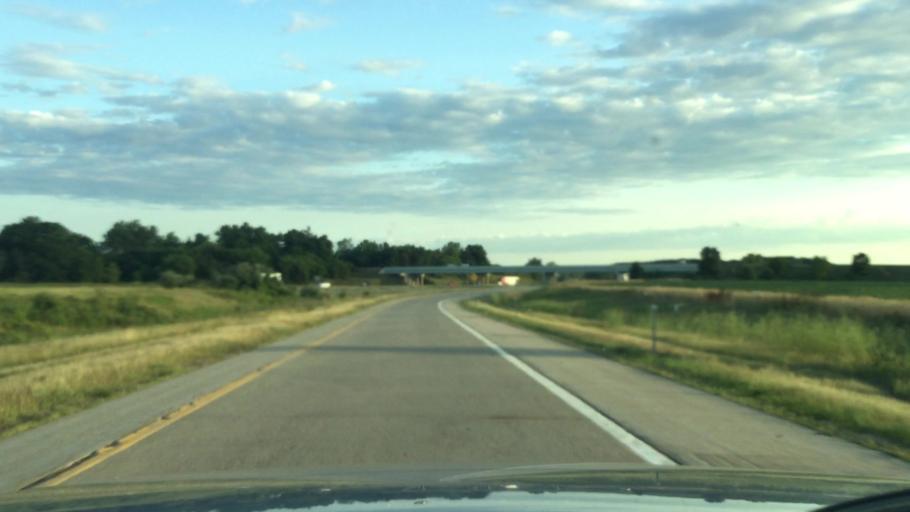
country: US
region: Michigan
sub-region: Clinton County
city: Bath
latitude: 42.8097
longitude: -84.5099
